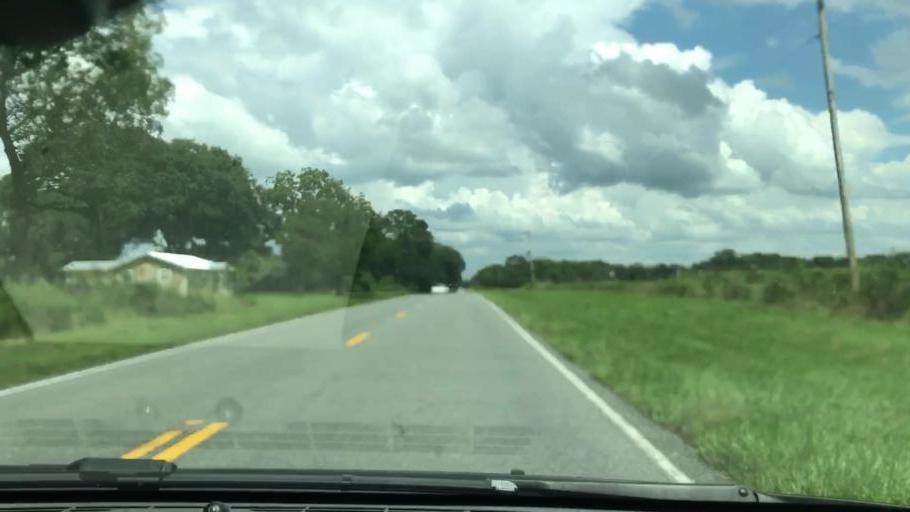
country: US
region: Florida
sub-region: Jackson County
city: Malone
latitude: 30.8953
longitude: -85.1420
